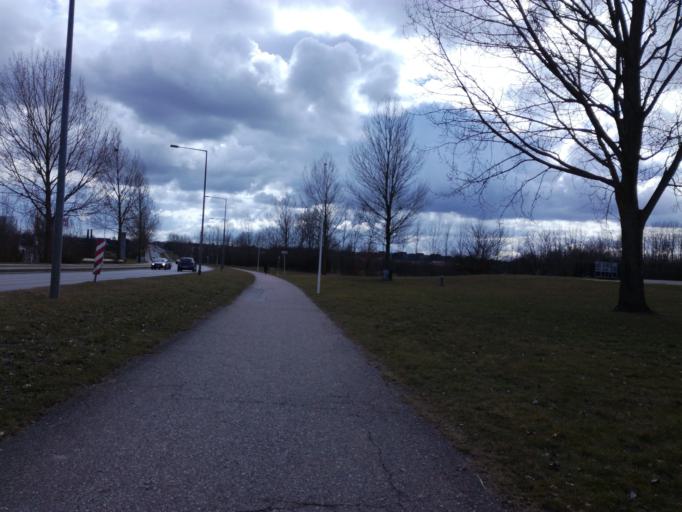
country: DK
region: South Denmark
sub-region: Fredericia Kommune
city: Fredericia
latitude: 55.5785
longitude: 9.7258
